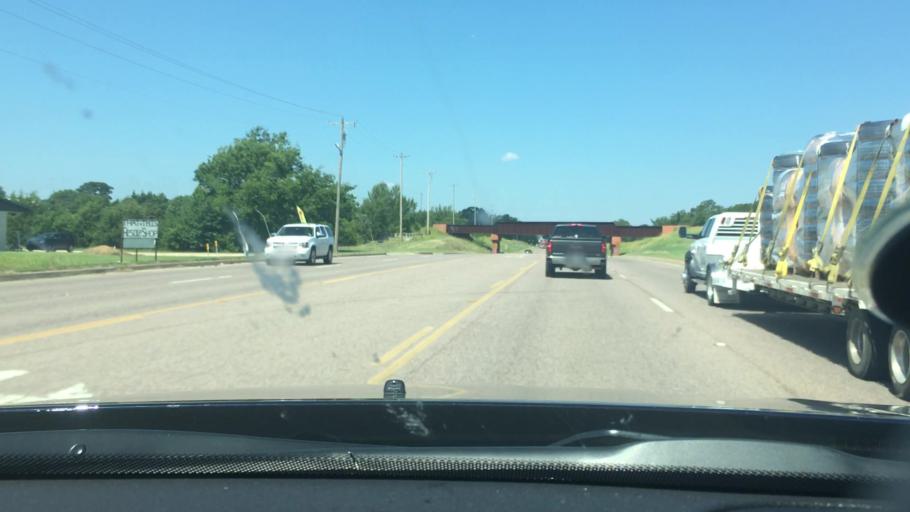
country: US
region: Oklahoma
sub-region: Bryan County
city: Calera
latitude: 33.9982
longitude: -96.5189
